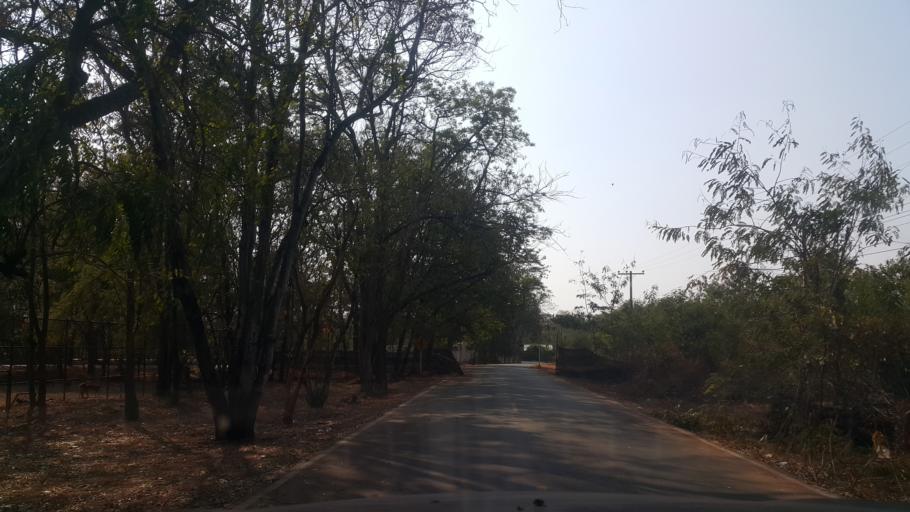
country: TH
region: Nakhon Ratchasima
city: Nakhon Ratchasima
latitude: 14.8568
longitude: 102.0871
